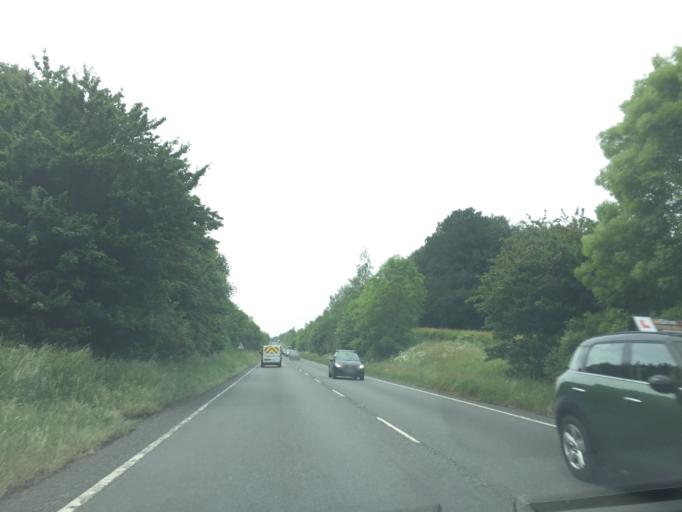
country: GB
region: England
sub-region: Hampshire
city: Four Marks
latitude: 51.0798
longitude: -1.1329
